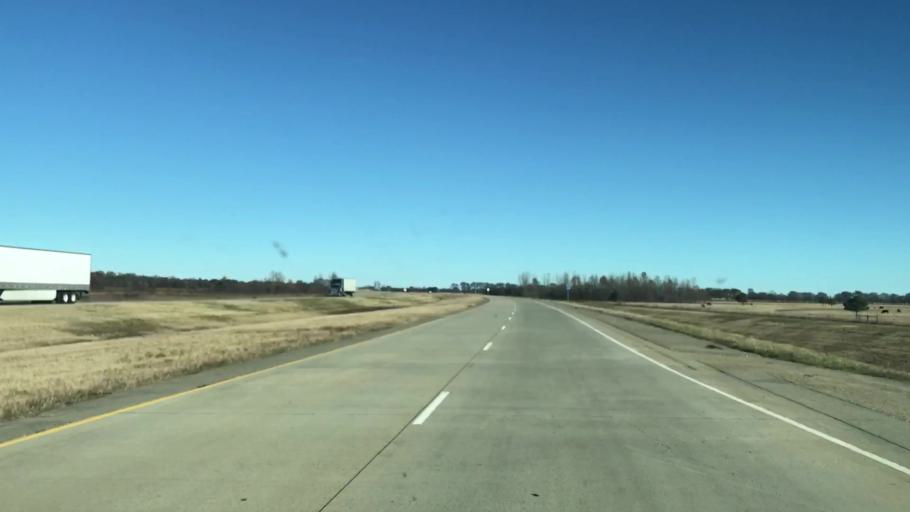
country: US
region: Louisiana
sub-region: Caddo Parish
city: Vivian
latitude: 32.8594
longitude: -93.8610
